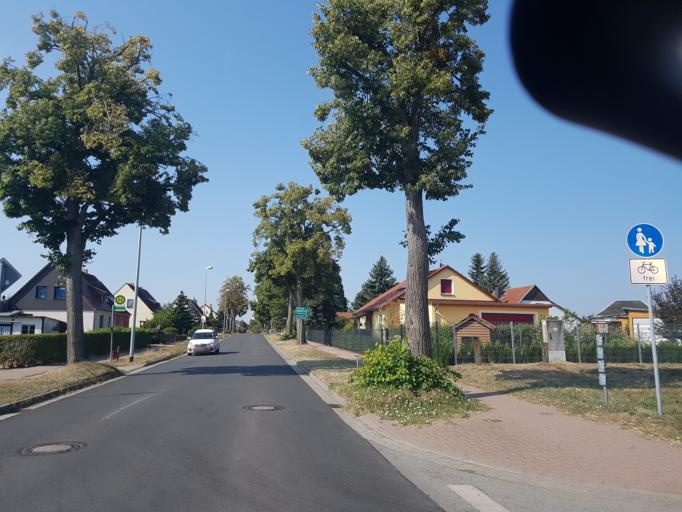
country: DE
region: Brandenburg
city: Wiesenburg
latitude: 52.1168
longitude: 12.4623
